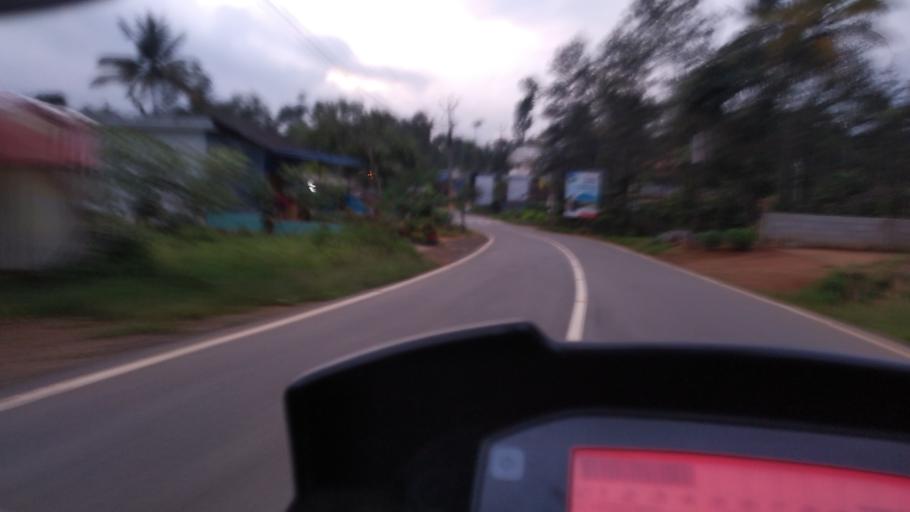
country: IN
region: Kerala
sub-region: Idukki
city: Munnar
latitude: 9.9690
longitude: 77.1304
